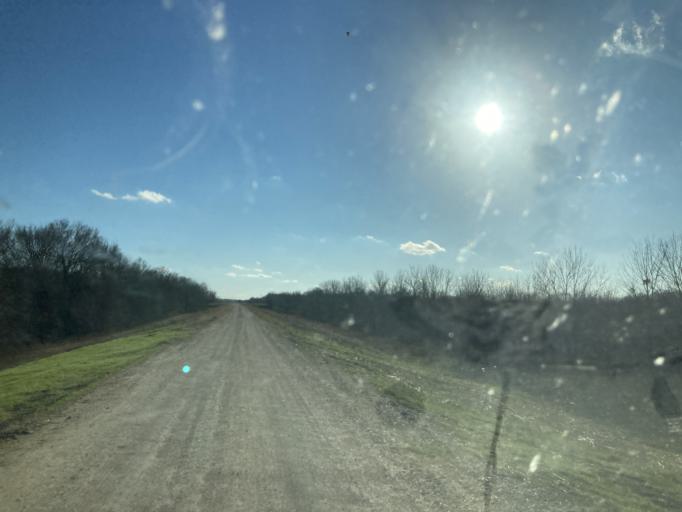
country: US
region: Mississippi
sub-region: Yazoo County
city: Yazoo City
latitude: 32.9211
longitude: -90.5527
